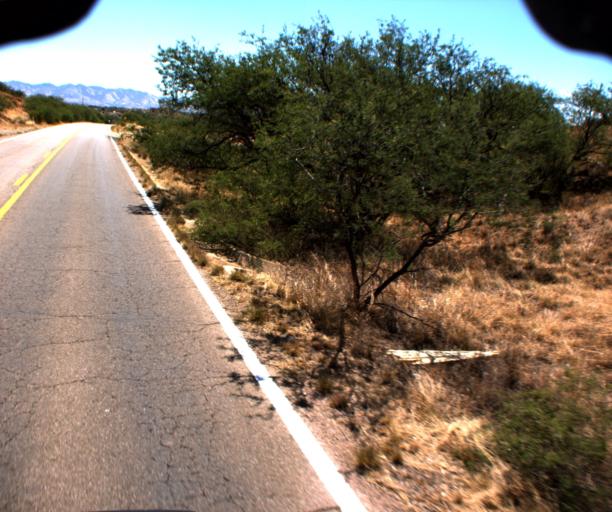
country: US
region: Arizona
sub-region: Santa Cruz County
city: Rio Rico
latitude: 31.4301
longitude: -110.9738
